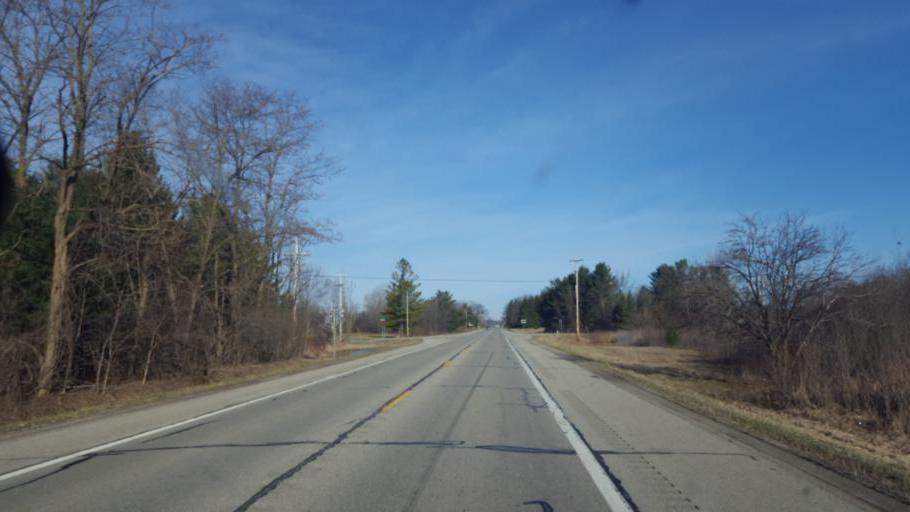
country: US
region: Michigan
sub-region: Montcalm County
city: Edmore
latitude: 43.4125
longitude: -85.1232
